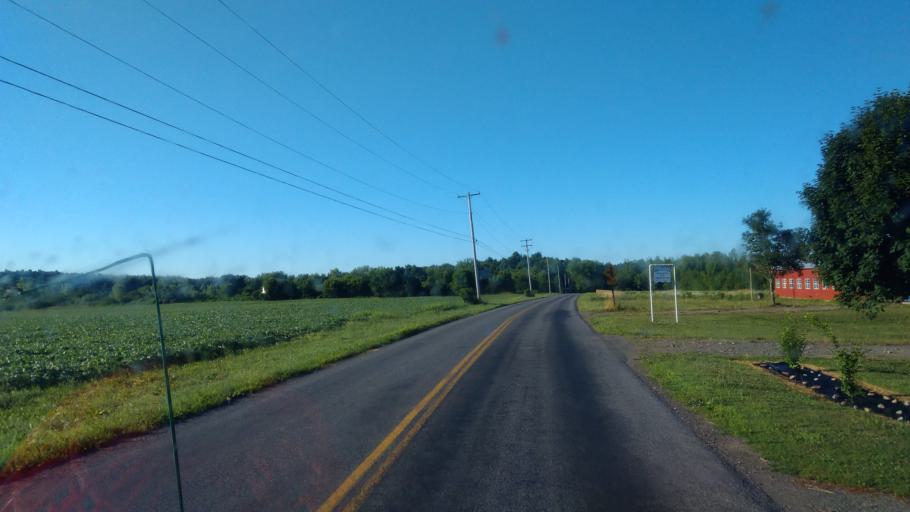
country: US
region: New York
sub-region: Wayne County
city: Lyons
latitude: 43.0955
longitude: -77.0234
